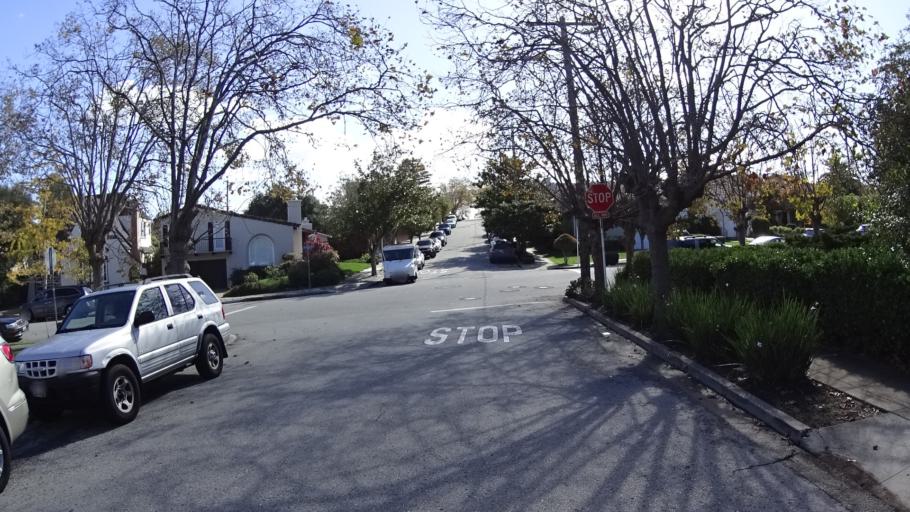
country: US
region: California
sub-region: San Mateo County
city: Millbrae
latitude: 37.6011
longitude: -122.3964
